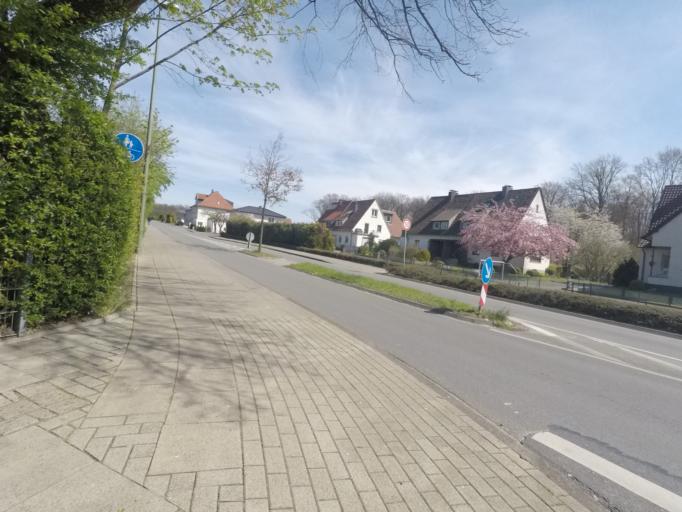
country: DE
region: North Rhine-Westphalia
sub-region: Regierungsbezirk Detmold
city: Leopoldshohe
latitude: 52.0355
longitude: 8.6375
